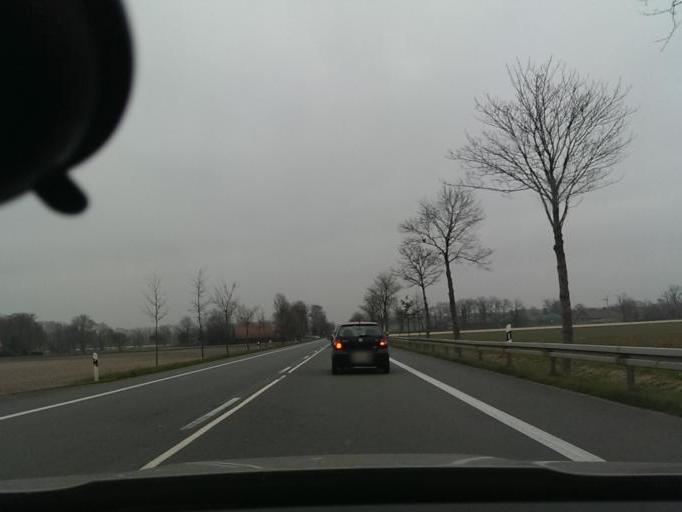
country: DE
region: North Rhine-Westphalia
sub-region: Regierungsbezirk Detmold
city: Delbruck
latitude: 51.7775
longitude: 8.5117
